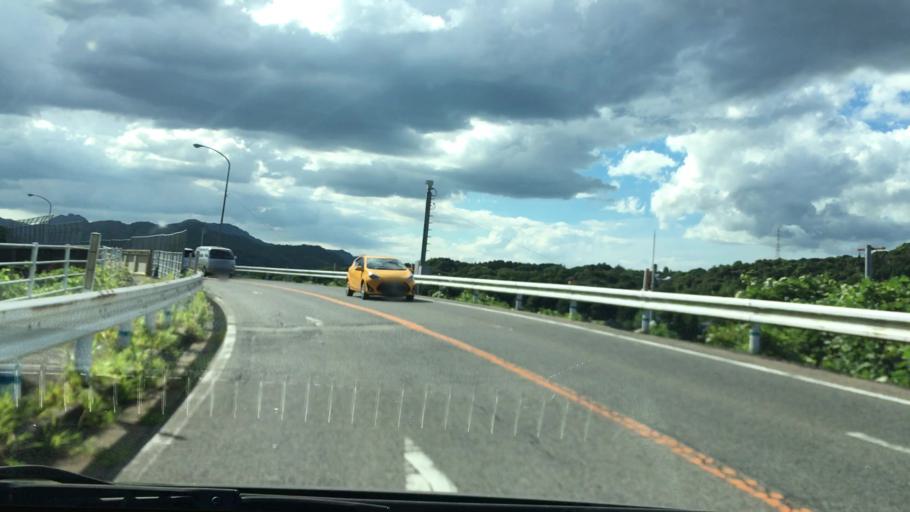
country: JP
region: Saga Prefecture
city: Takeocho-takeo
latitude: 33.1958
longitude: 129.9781
